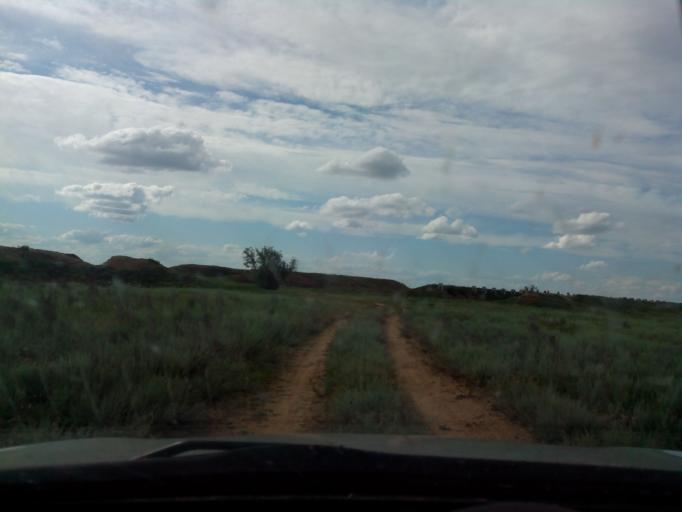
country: RU
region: Volgograd
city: Leninsk
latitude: 48.6803
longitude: 45.3699
